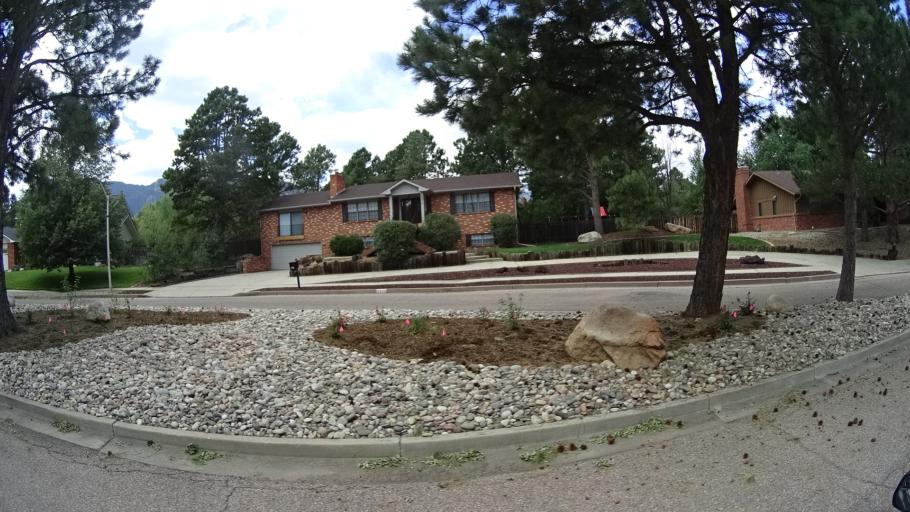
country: US
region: Colorado
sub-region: El Paso County
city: Colorado Springs
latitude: 38.7887
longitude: -104.8261
